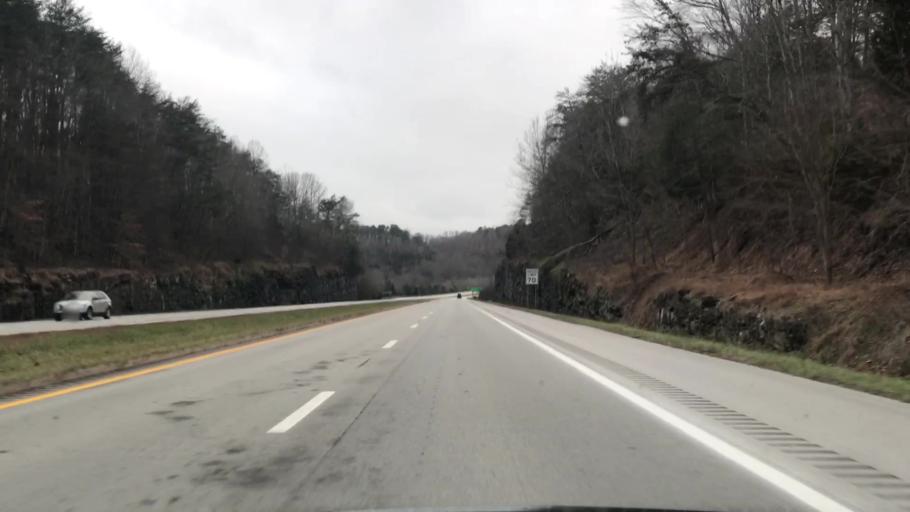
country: US
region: Kentucky
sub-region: Russell County
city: Russell Springs
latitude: 37.0909
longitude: -84.8816
